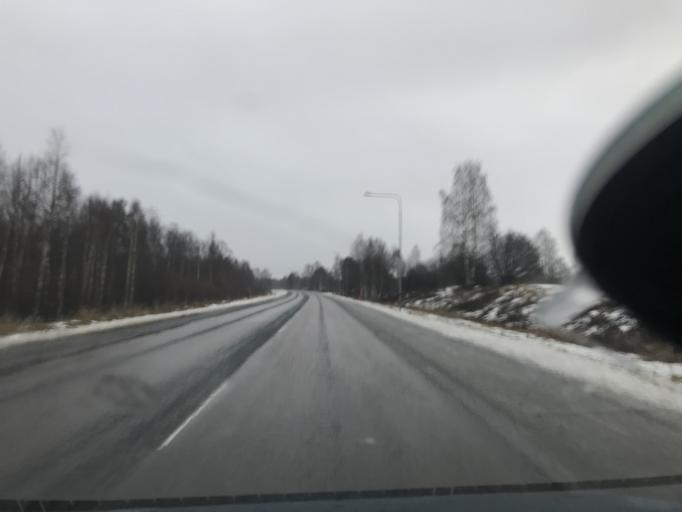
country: SE
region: Norrbotten
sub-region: Lulea Kommun
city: Sodra Sunderbyn
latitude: 65.6586
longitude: 21.9578
